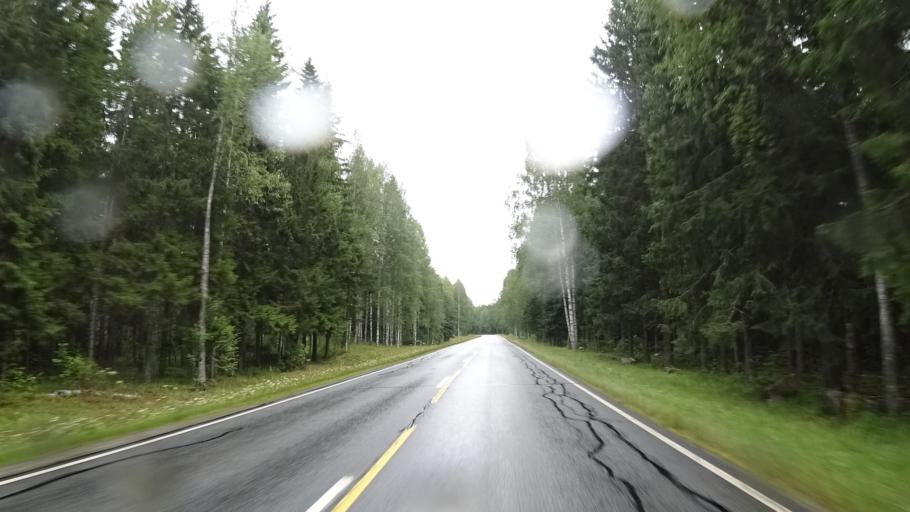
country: FI
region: North Karelia
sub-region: Keski-Karjala
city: Kesaelahti
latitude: 62.1080
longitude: 29.7821
